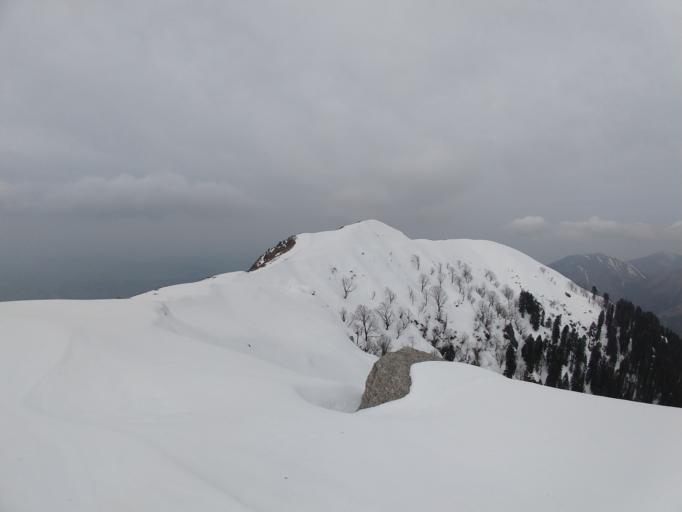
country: IN
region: Himachal Pradesh
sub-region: Kangra
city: Palampur
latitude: 32.1830
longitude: 76.5121
